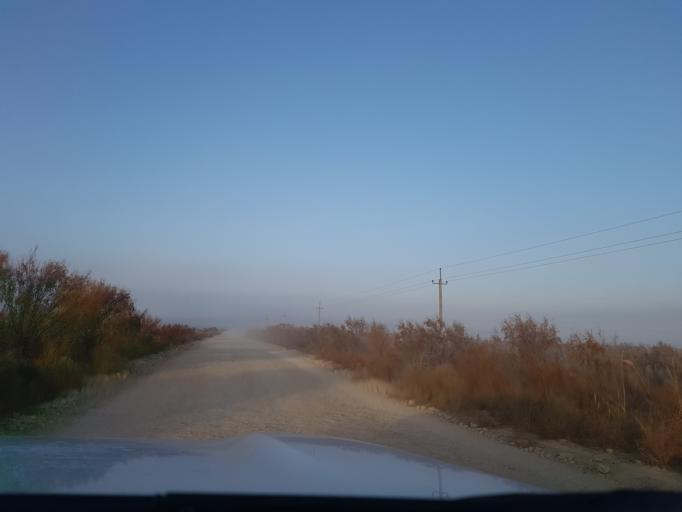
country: TM
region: Dasoguz
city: Koeneuergench
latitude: 41.8448
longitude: 58.5052
